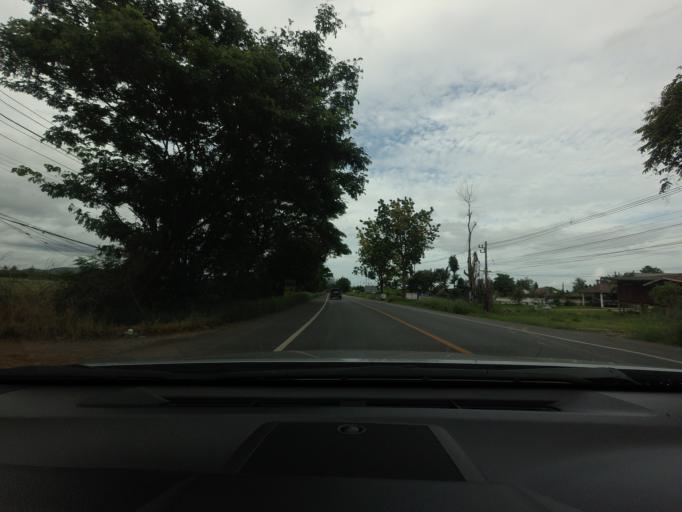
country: TH
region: Prachuap Khiri Khan
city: Hua Hin
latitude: 12.5815
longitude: 99.8526
